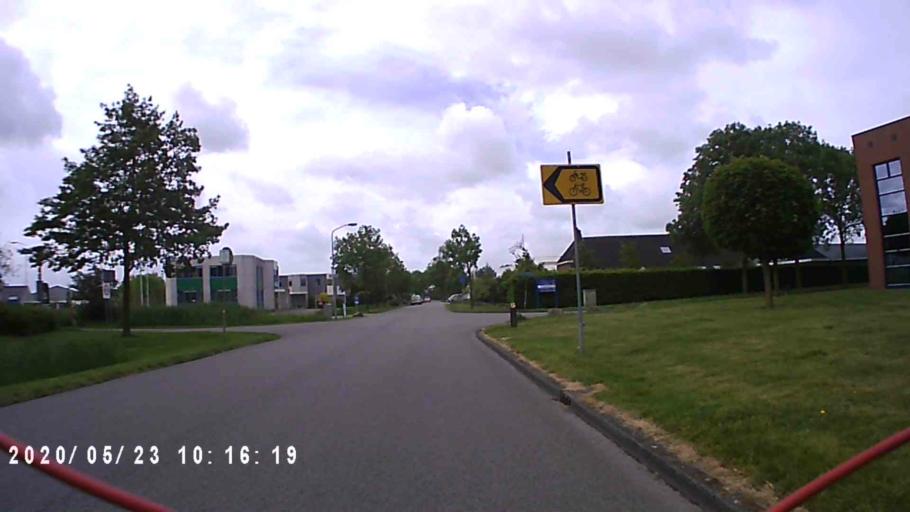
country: NL
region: Groningen
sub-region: Gemeente Appingedam
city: Appingedam
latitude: 53.3095
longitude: 6.8544
